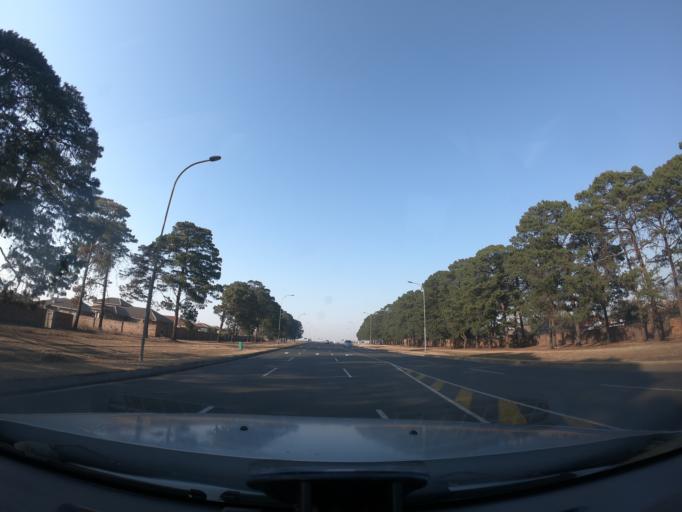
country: ZA
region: Mpumalanga
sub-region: Nkangala District Municipality
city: Middelburg
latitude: -25.8008
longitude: 29.4621
